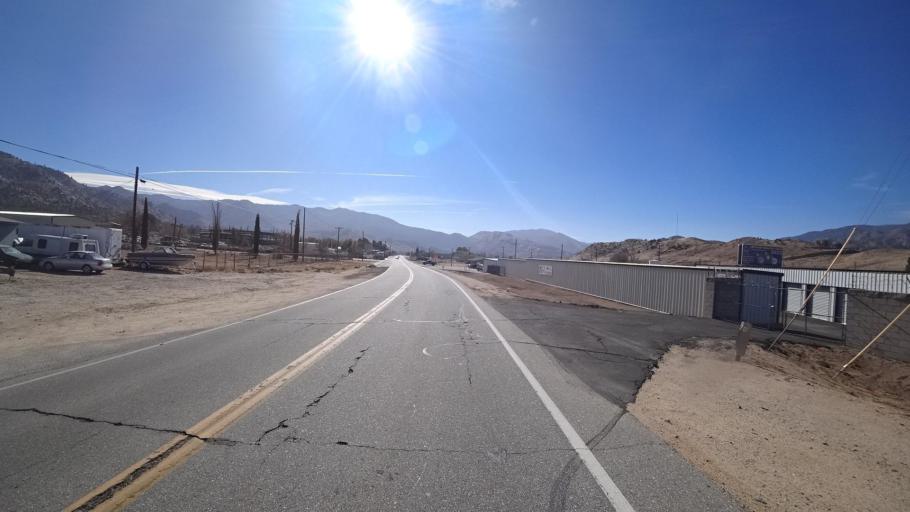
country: US
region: California
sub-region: Kern County
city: Lake Isabella
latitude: 35.6346
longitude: -118.4718
